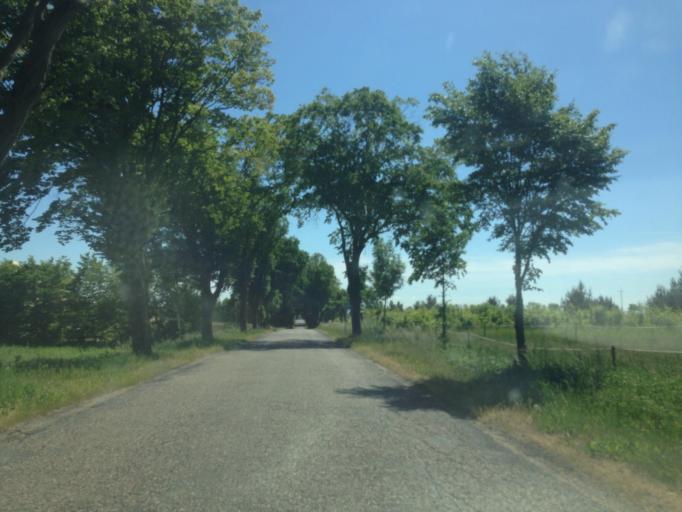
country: PL
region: Kujawsko-Pomorskie
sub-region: Powiat brodnicki
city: Gorzno
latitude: 53.2170
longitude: 19.6347
